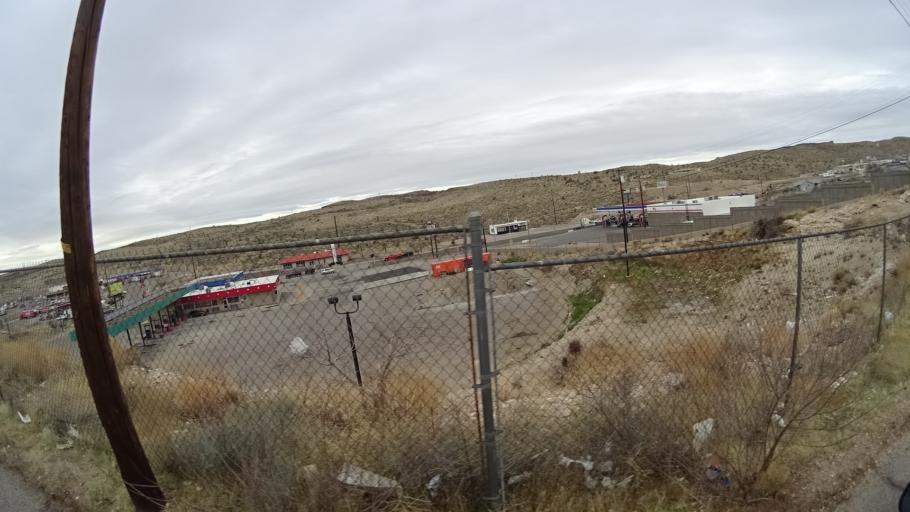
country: US
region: Arizona
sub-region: Mohave County
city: Kingman
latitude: 35.1936
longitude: -114.0698
